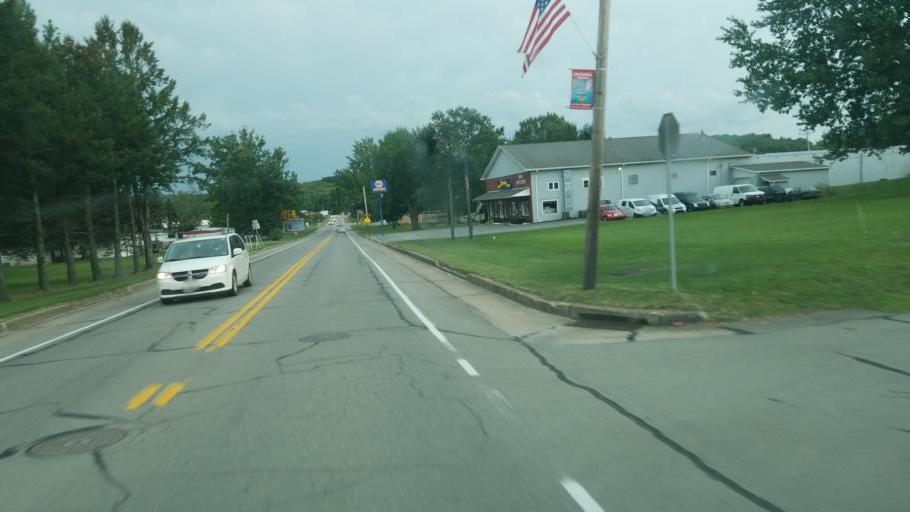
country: US
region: Pennsylvania
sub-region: Clarion County
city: Knox
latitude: 41.2326
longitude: -79.5285
